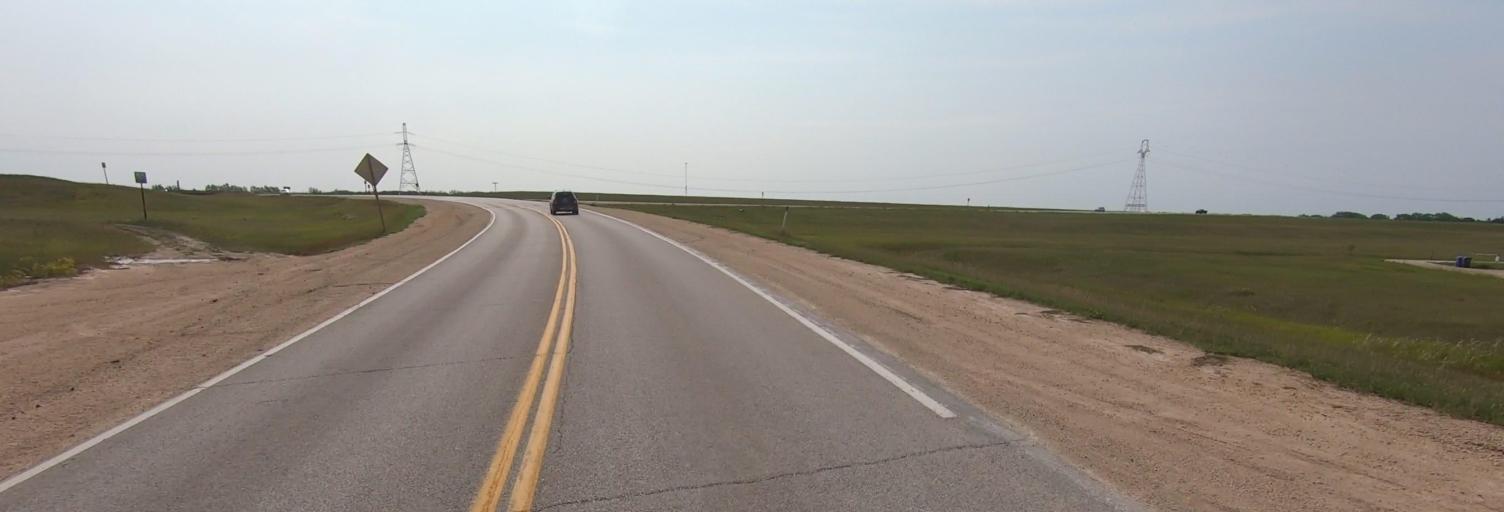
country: CA
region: Manitoba
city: Winnipeg
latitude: 49.7587
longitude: -97.1268
